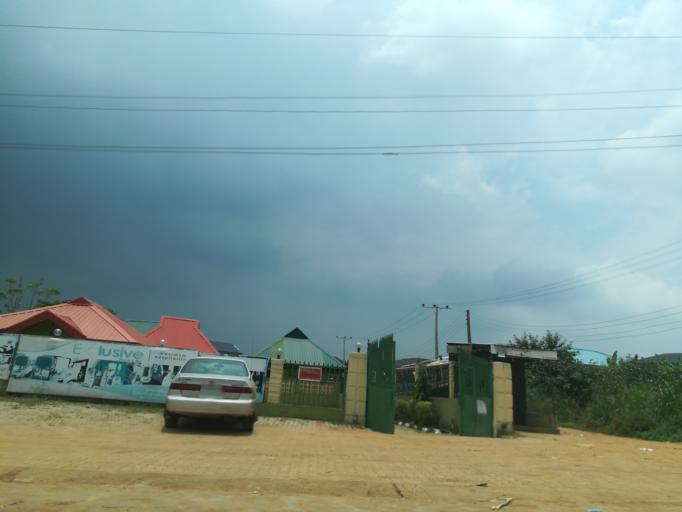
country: NG
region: Lagos
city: Ikorodu
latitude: 6.6115
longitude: 3.5800
